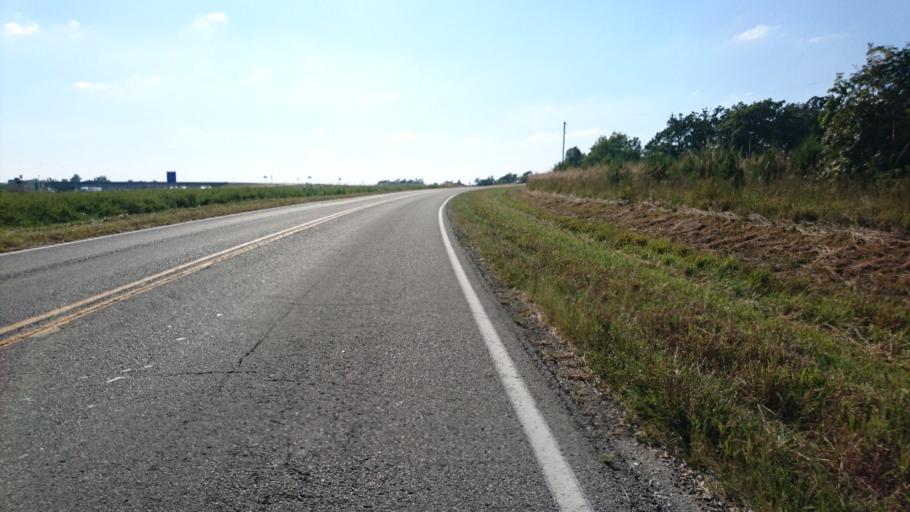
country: US
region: Missouri
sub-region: Laclede County
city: Lebanon
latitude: 37.6017
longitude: -92.7129
